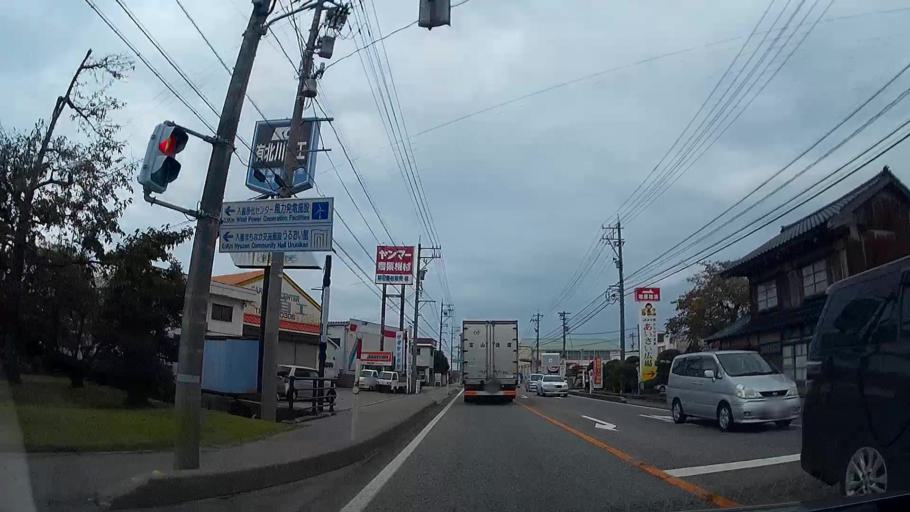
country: JP
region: Toyama
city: Nyuzen
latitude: 36.9333
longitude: 137.5030
